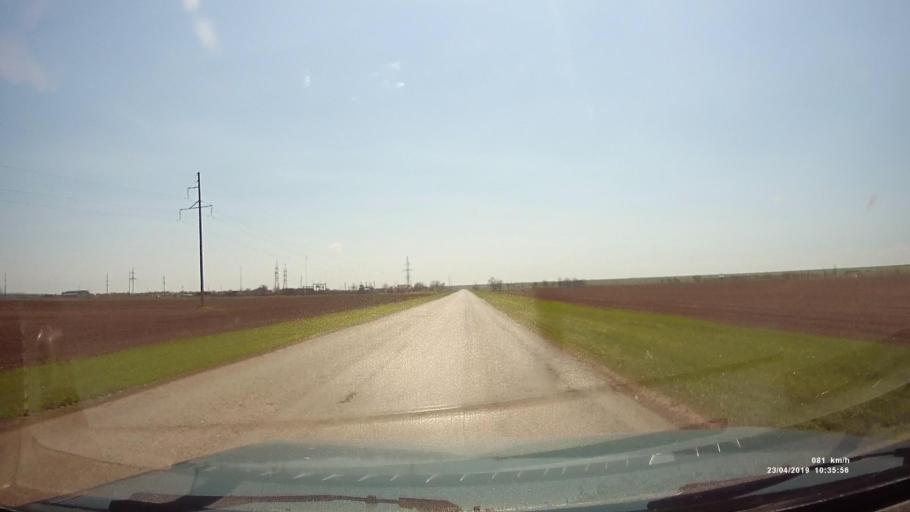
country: RU
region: Kalmykiya
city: Yashalta
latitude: 46.5494
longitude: 42.6302
